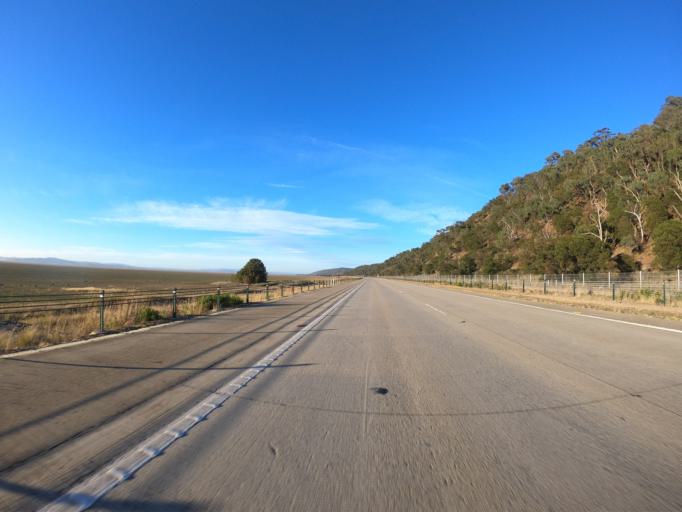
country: AU
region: New South Wales
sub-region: Yass Valley
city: Gundaroo
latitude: -35.0795
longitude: 149.3747
